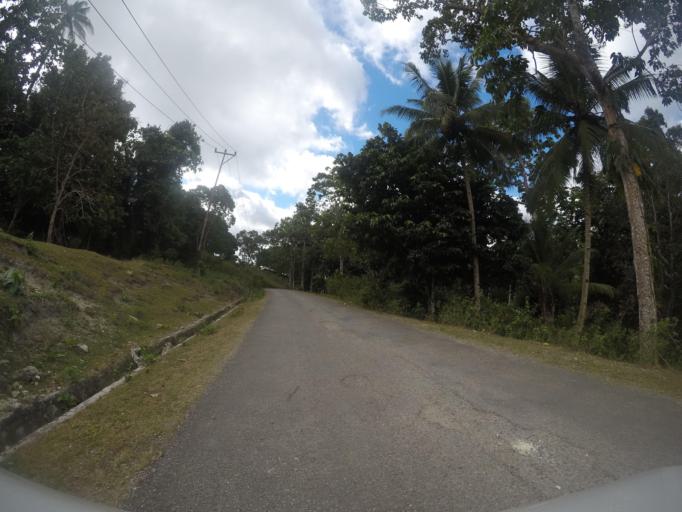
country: TL
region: Lautem
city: Lospalos
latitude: -8.5341
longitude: 126.9159
